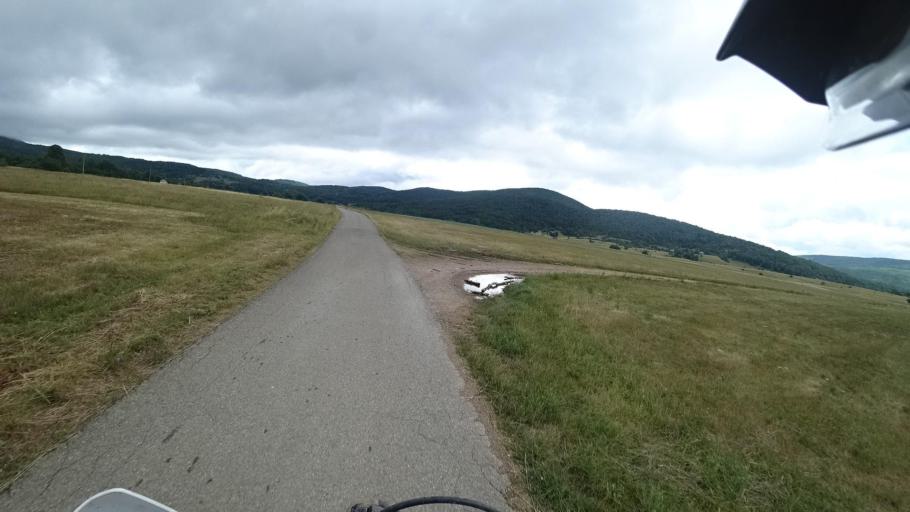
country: HR
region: Licko-Senjska
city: Jezerce
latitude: 44.7839
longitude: 15.5023
